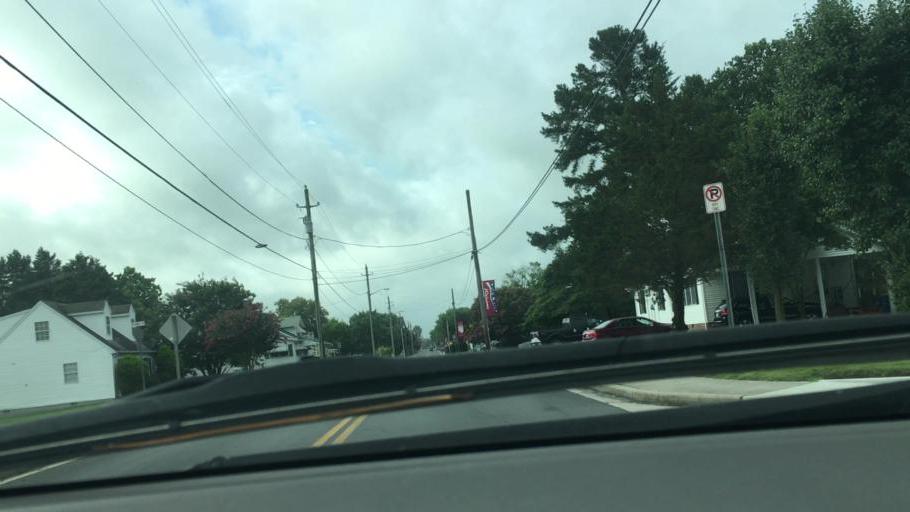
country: US
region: Maryland
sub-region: Wicomico County
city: Fruitland
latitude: 38.3268
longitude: -75.6230
